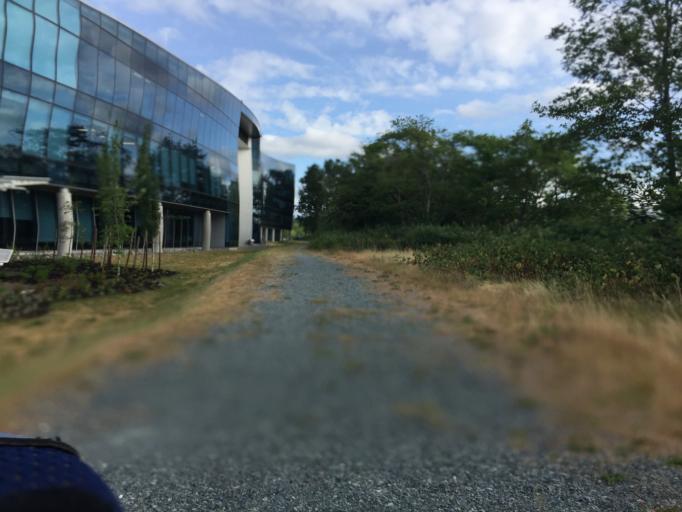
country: CA
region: British Columbia
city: Richmond
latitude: 49.1849
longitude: -123.1432
